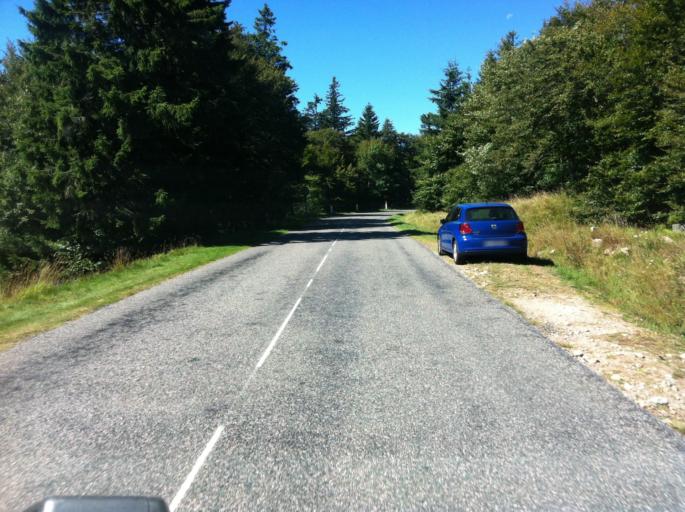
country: FR
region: Alsace
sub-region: Departement du Haut-Rhin
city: Soultzeren
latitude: 48.1130
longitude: 7.0606
